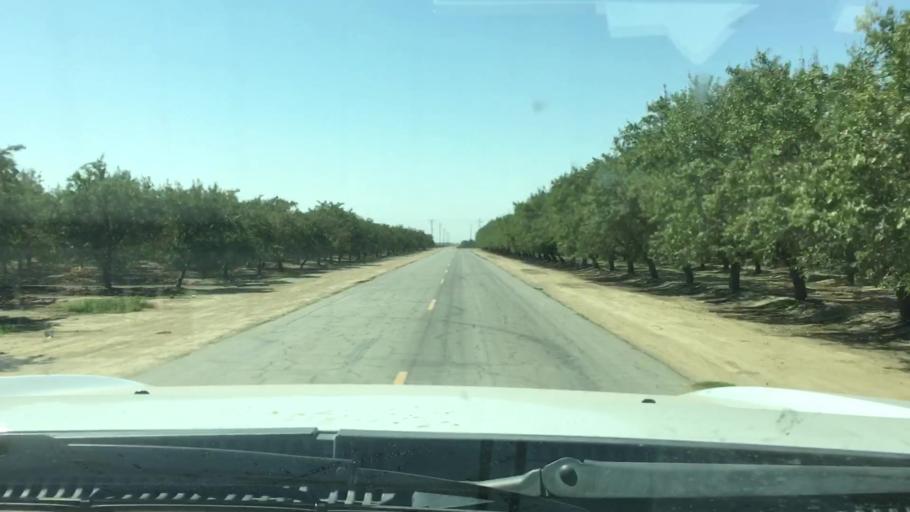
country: US
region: California
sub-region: Kern County
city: Shafter
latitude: 35.4781
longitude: -119.3109
